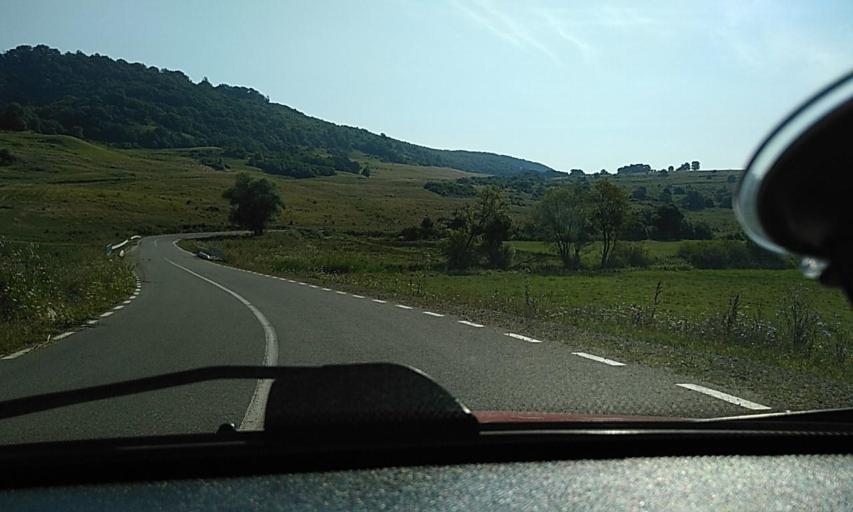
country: RO
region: Brasov
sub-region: Comuna Bunesti
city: Bunesti
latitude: 46.0825
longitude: 25.0627
